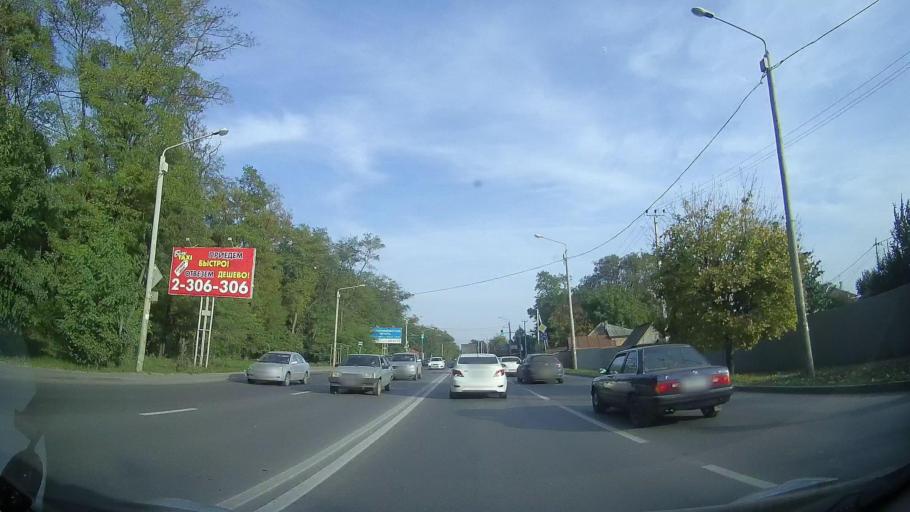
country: RU
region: Rostov
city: Imeni Chkalova
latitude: 47.2750
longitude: 39.7920
